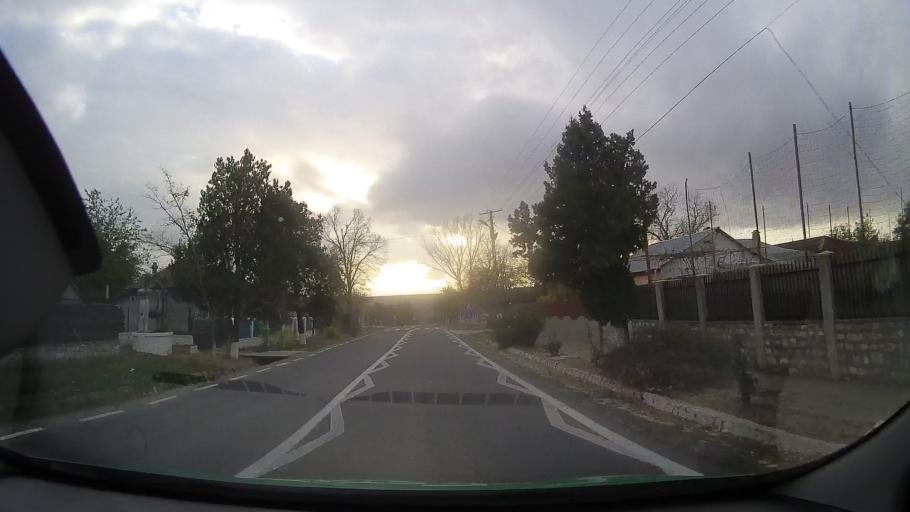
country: RO
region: Constanta
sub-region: Comuna Adamclisi
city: Adamclisi
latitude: 44.0836
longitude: 27.9560
